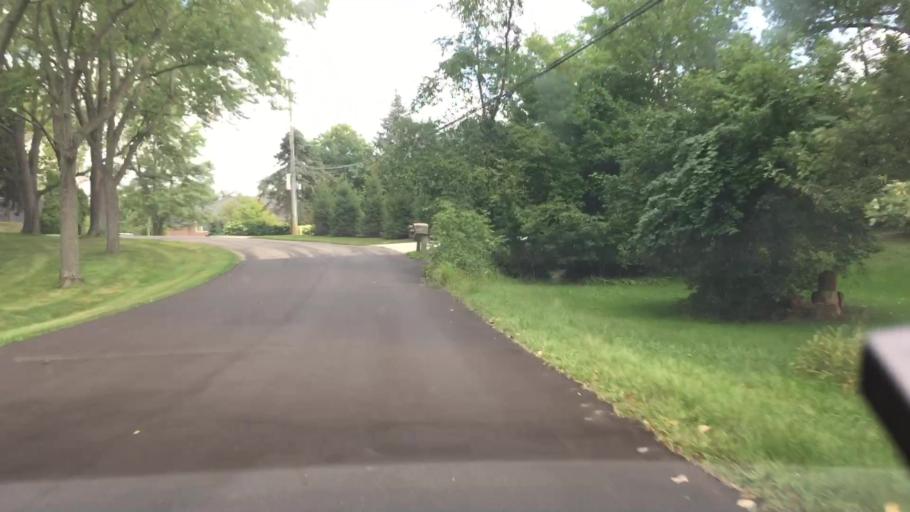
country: US
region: Michigan
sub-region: Oakland County
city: Orchard Lake
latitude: 42.5682
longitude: -83.3213
